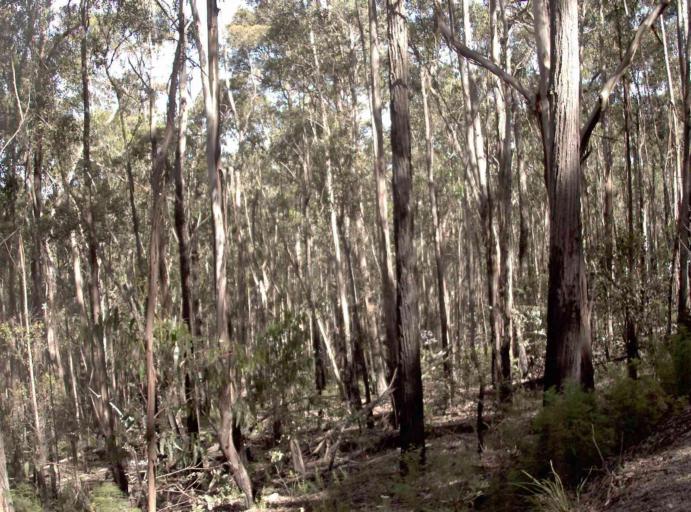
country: AU
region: Victoria
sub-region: East Gippsland
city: Lakes Entrance
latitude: -37.4077
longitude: 148.1224
